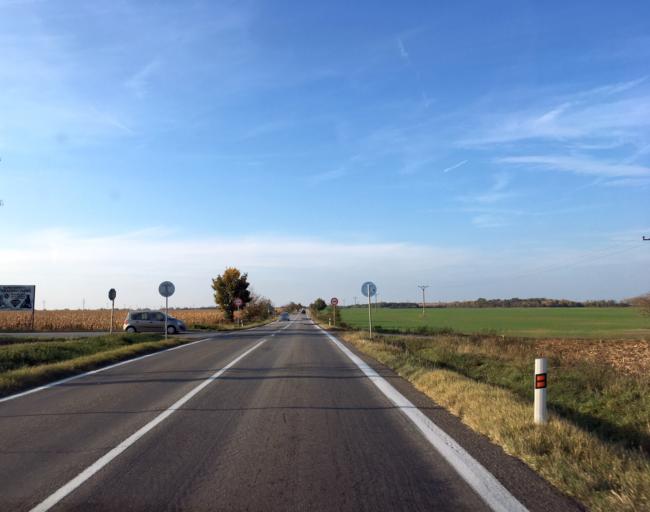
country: SK
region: Nitriansky
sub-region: Okres Nove Zamky
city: Nove Zamky
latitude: 48.0395
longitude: 18.1233
